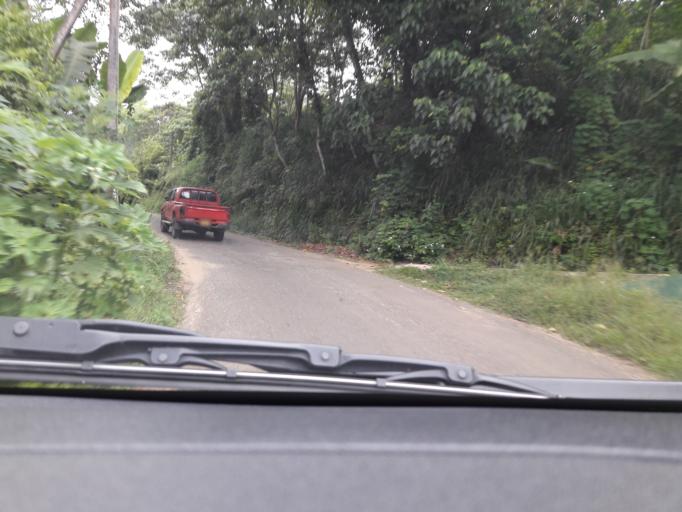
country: LK
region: Southern
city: Galle
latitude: 6.1940
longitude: 80.3037
